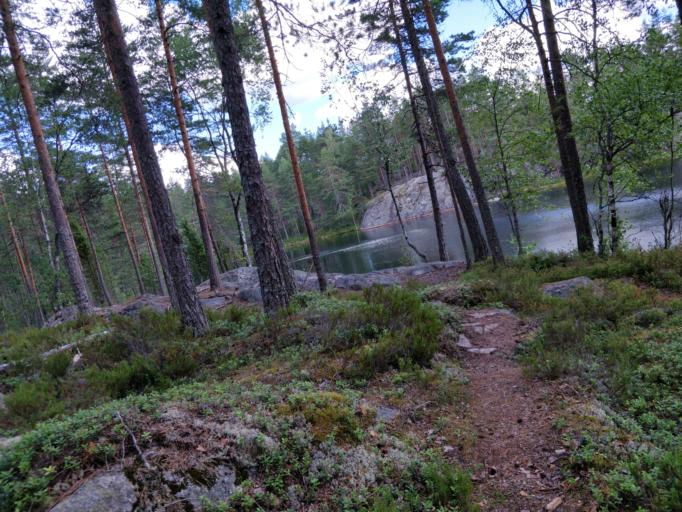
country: FI
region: Uusimaa
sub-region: Helsinki
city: Vihti
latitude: 60.3110
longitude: 24.4774
